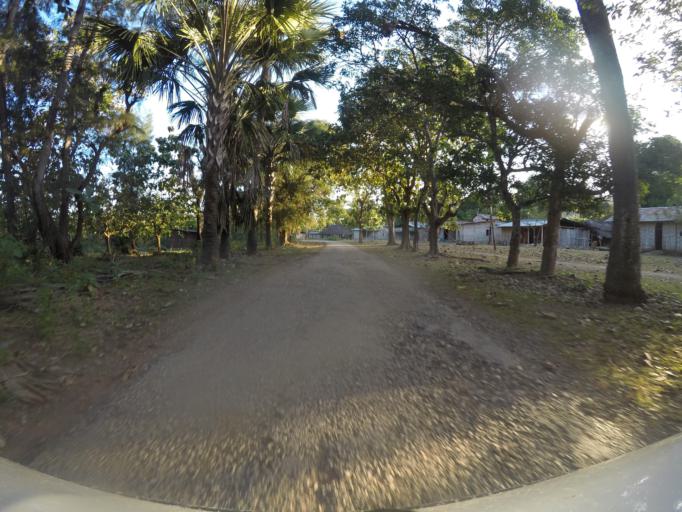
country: TL
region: Baucau
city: Venilale
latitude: -8.7369
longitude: 126.7149
